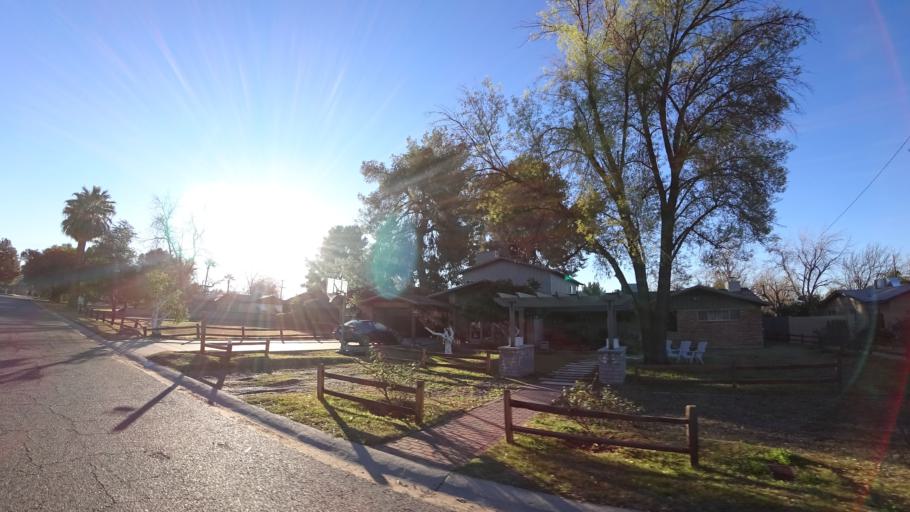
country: US
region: Arizona
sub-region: Maricopa County
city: Phoenix
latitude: 33.4903
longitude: -112.0098
